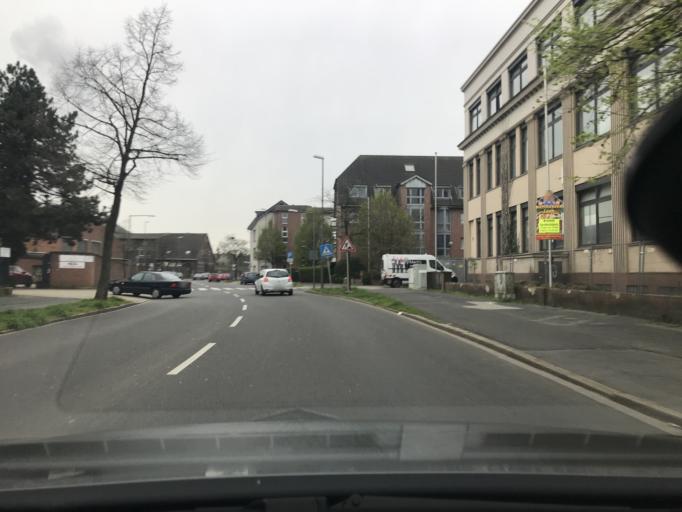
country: DE
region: North Rhine-Westphalia
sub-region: Regierungsbezirk Dusseldorf
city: Krefeld
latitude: 51.3574
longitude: 6.6421
